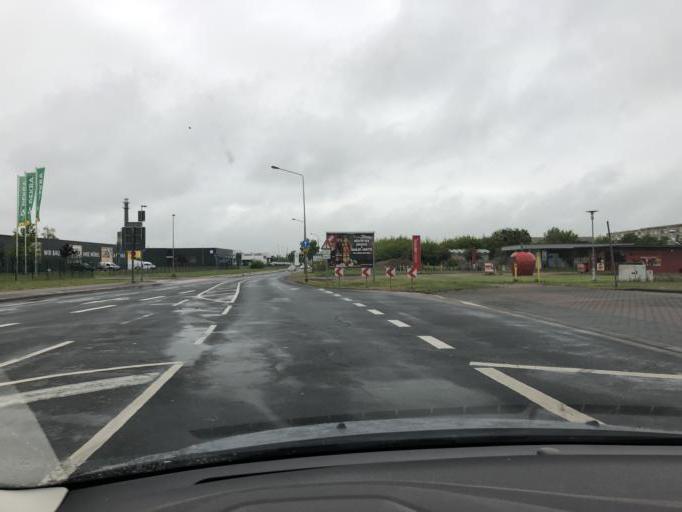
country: DE
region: Saxony-Anhalt
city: Dessau
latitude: 51.8261
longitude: 12.2152
